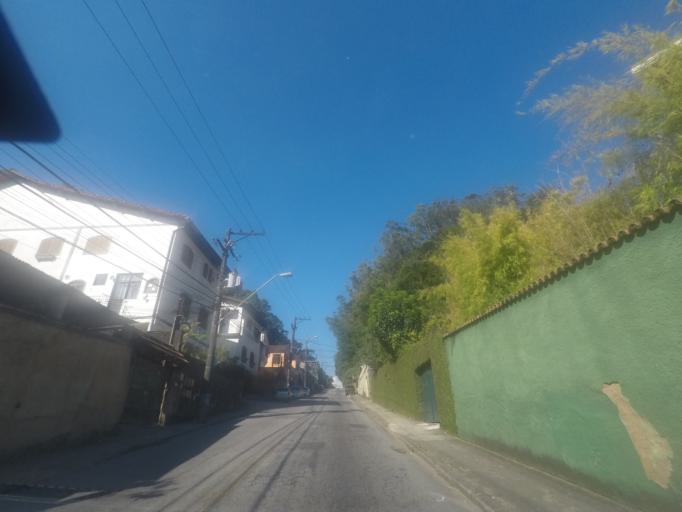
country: BR
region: Rio de Janeiro
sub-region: Petropolis
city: Petropolis
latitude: -22.5316
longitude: -43.1934
